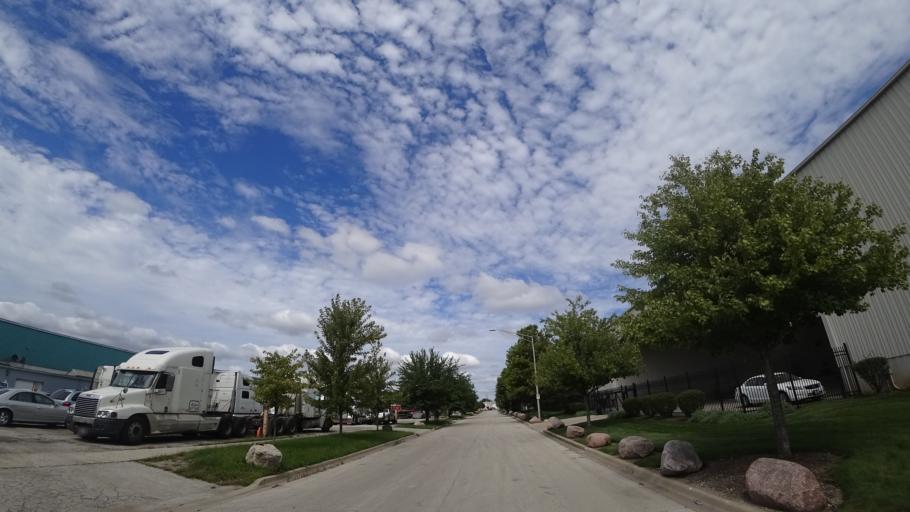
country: US
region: Illinois
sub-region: Cook County
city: Chicago Ridge
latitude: 41.7087
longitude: -87.7891
